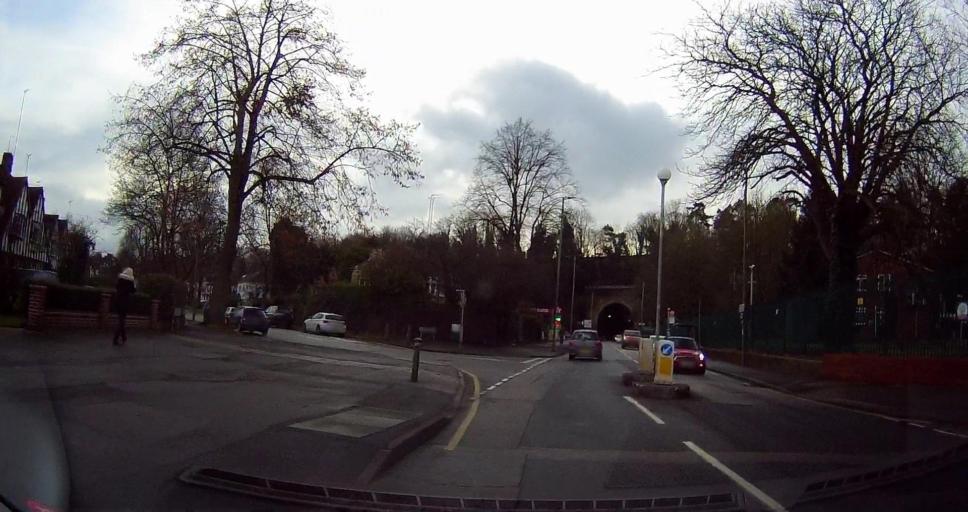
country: GB
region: England
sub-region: Greater London
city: Orpington
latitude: 51.3681
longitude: 0.0958
